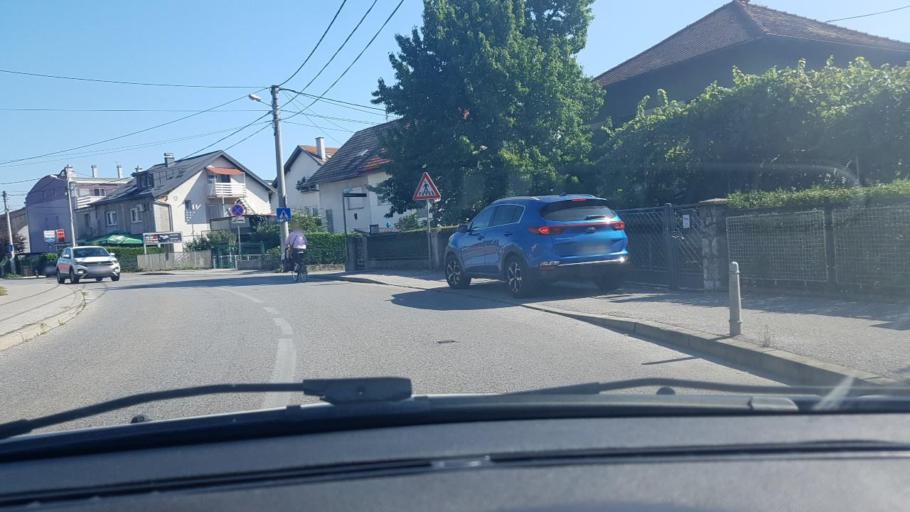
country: HR
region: Grad Zagreb
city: Dubrava
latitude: 45.8227
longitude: 16.0401
